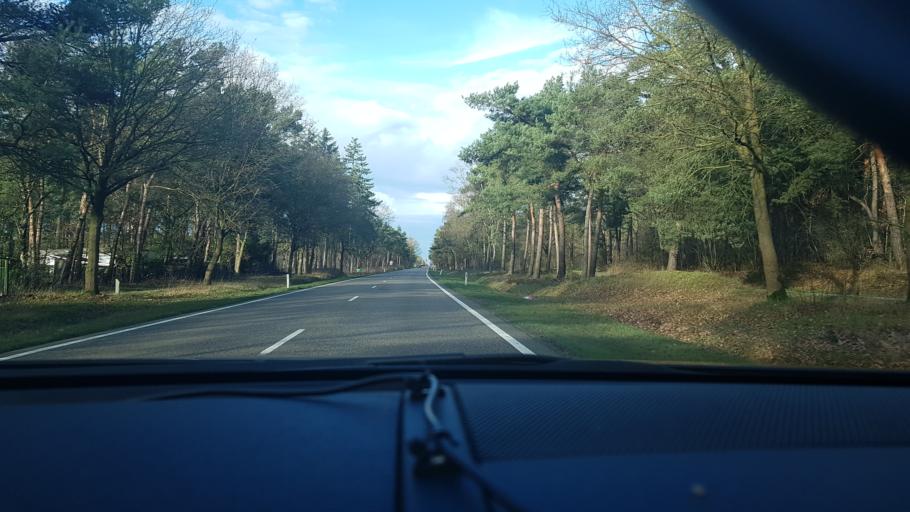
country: NL
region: Limburg
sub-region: Gemeente Peel en Maas
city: Maasbree
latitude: 51.3859
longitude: 5.9792
